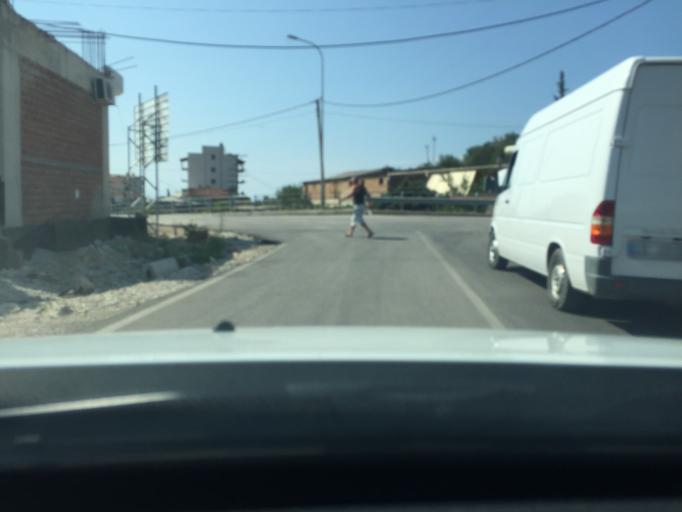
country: AL
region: Vlore
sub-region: Rrethi i Vlores
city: Himare
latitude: 40.1077
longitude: 19.7420
